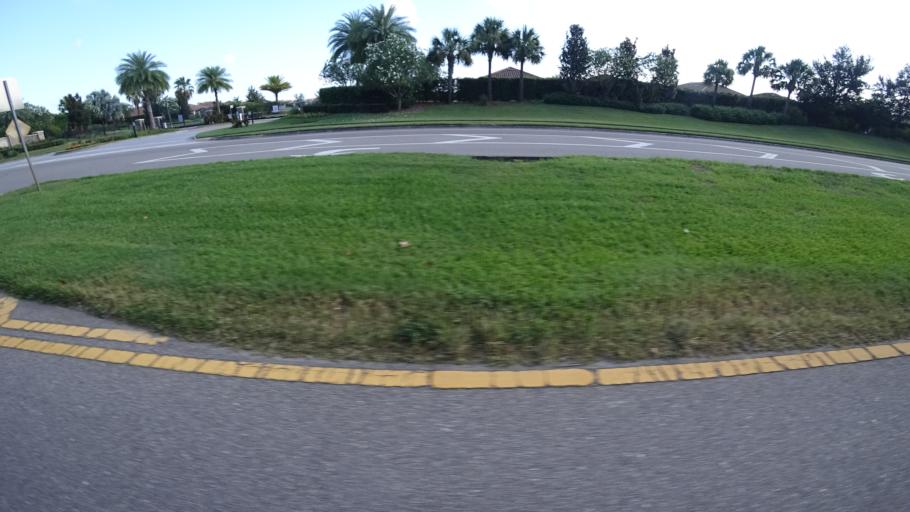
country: US
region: Florida
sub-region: Manatee County
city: Ellenton
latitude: 27.5059
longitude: -82.4773
